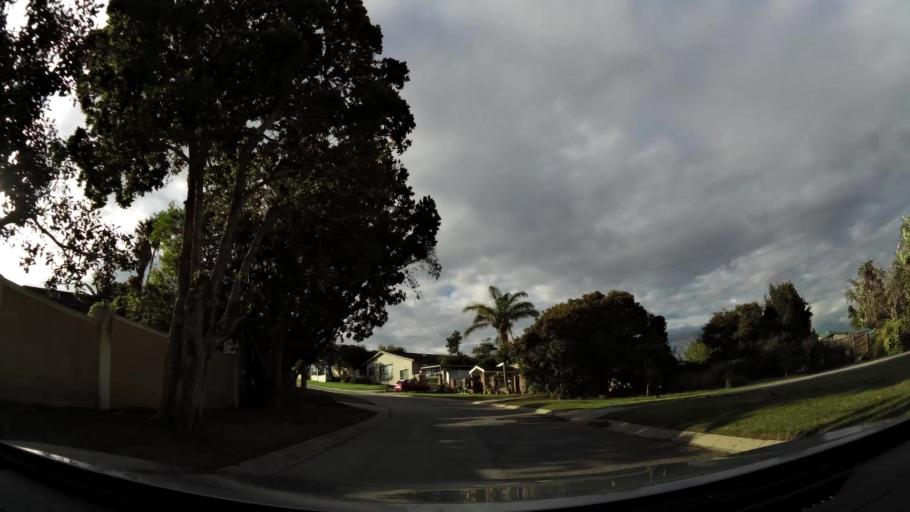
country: ZA
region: Eastern Cape
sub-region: Nelson Mandela Bay Metropolitan Municipality
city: Port Elizabeth
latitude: -33.9492
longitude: 25.4803
